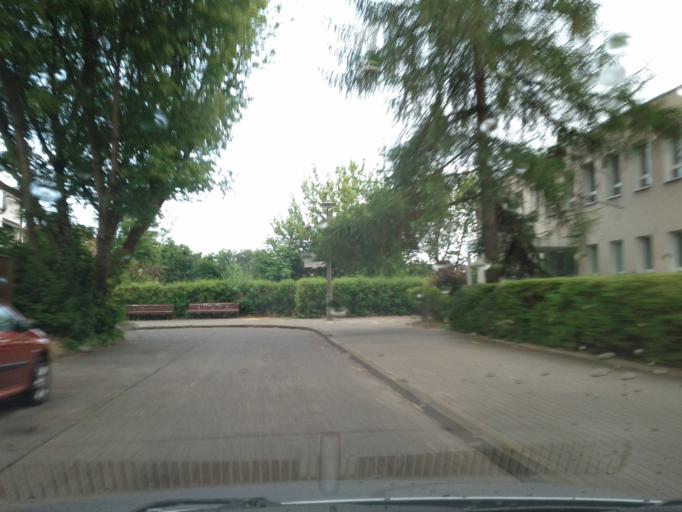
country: DE
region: Berlin
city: Adlershof
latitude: 52.4398
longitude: 13.5442
